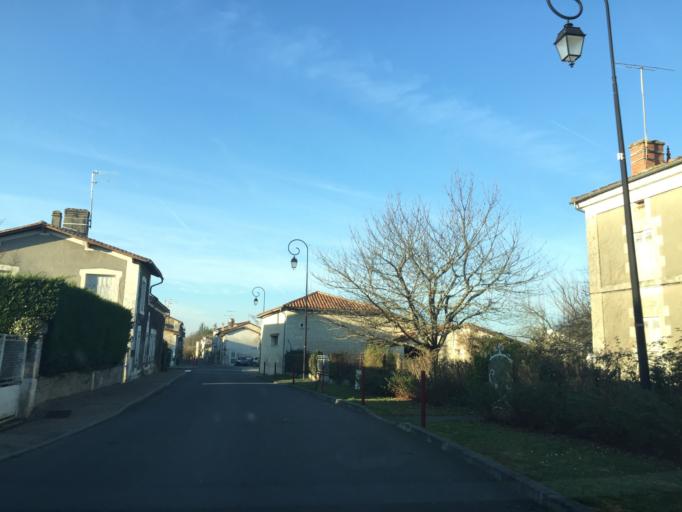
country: FR
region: Aquitaine
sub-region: Departement de la Dordogne
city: Saint-Aulaye
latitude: 45.2549
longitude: 0.2002
